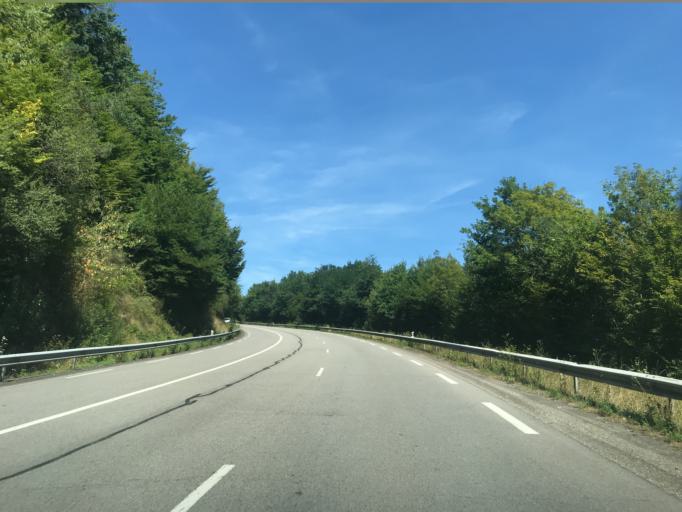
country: FR
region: Limousin
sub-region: Departement de la Correze
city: Tulle
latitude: 45.2660
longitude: 1.7914
